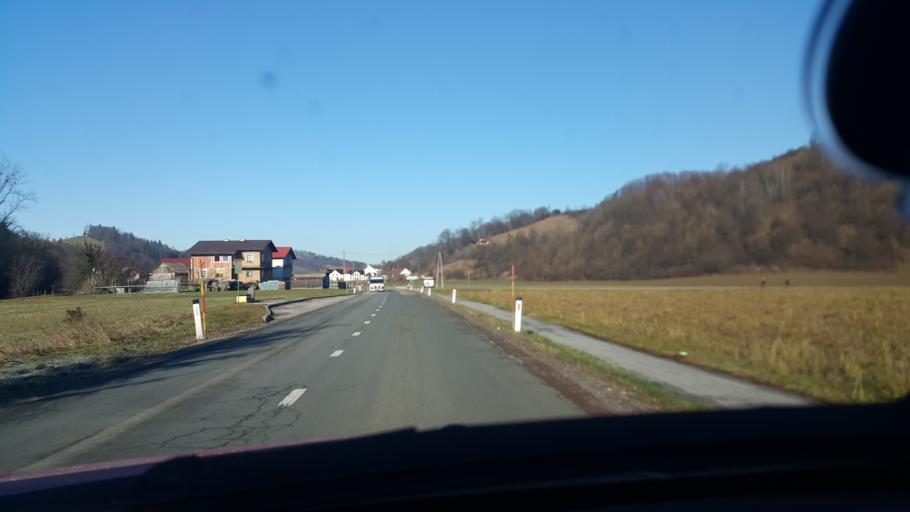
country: SI
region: Kungota
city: Zgornja Kungota
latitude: 46.6261
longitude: 15.6313
